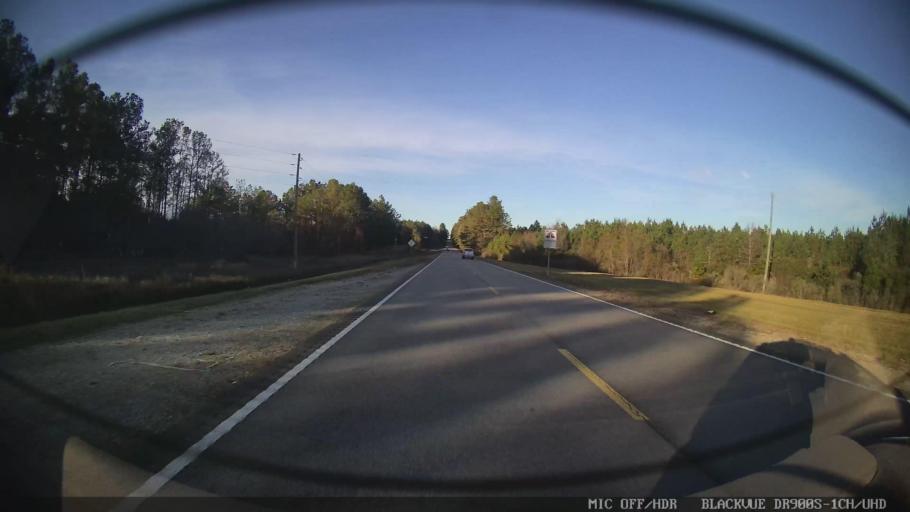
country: US
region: Mississippi
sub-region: Lamar County
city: Purvis
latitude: 31.0867
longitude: -89.4164
